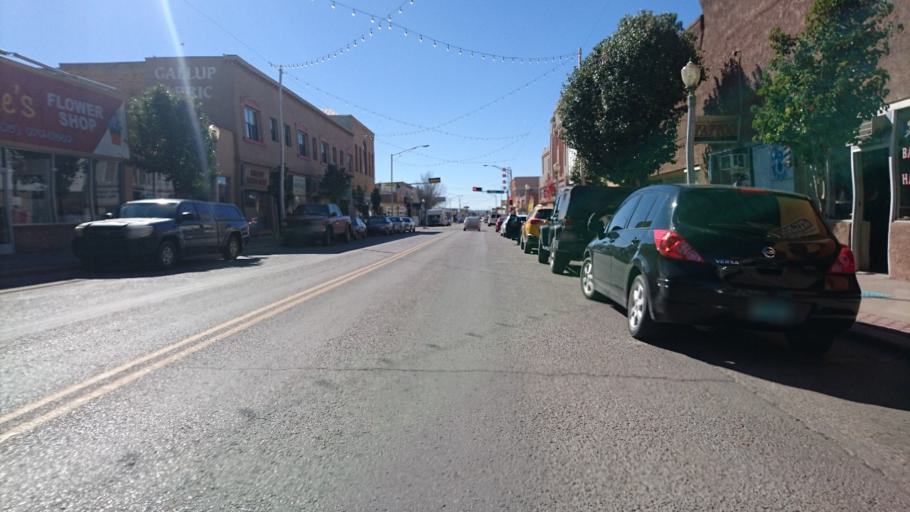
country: US
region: New Mexico
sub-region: McKinley County
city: Gallup
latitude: 35.5270
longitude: -108.7433
